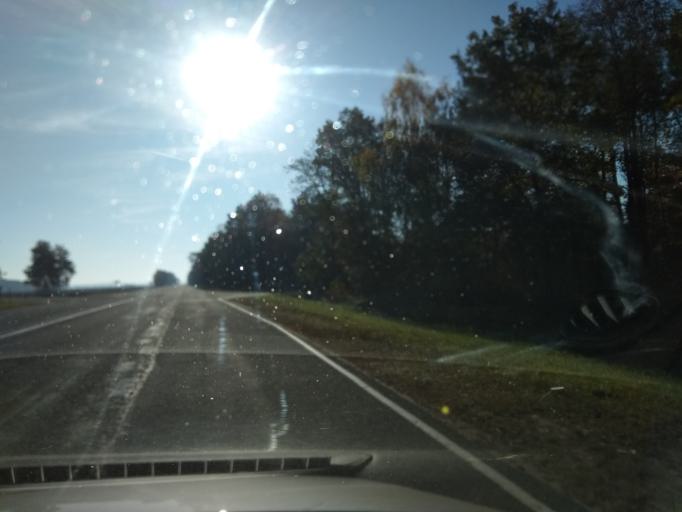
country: BY
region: Brest
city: Malaryta
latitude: 51.8727
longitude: 24.1784
